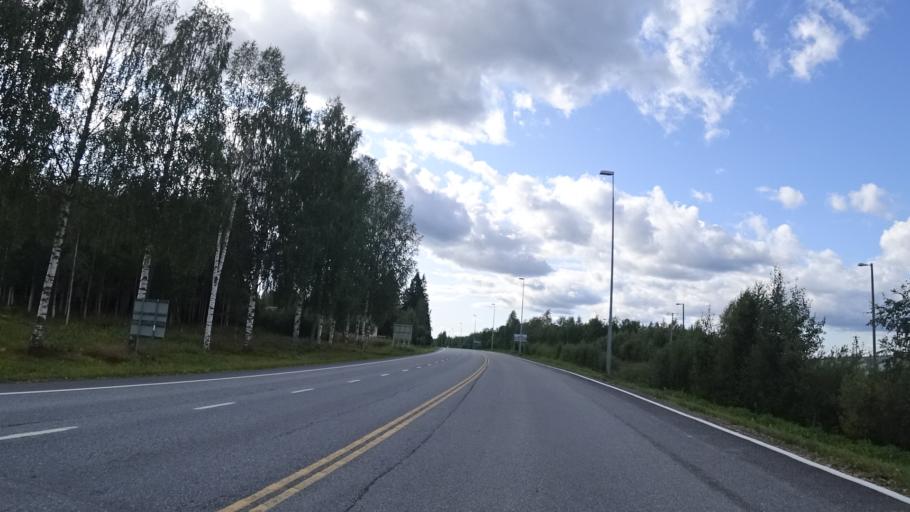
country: RU
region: Republic of Karelia
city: Vyartsilya
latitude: 62.1763
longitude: 30.5886
